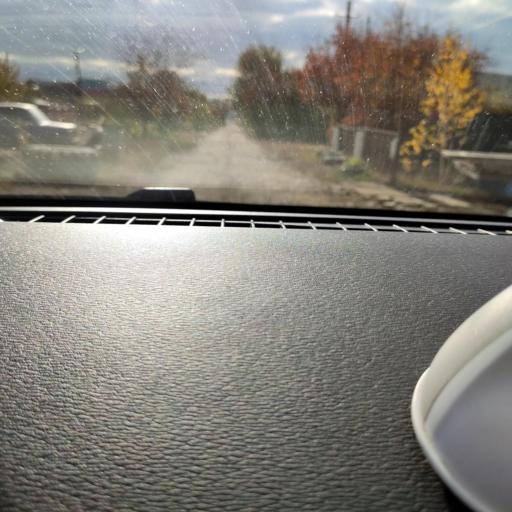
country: RU
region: Samara
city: Petra-Dubrava
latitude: 53.2481
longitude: 50.3143
